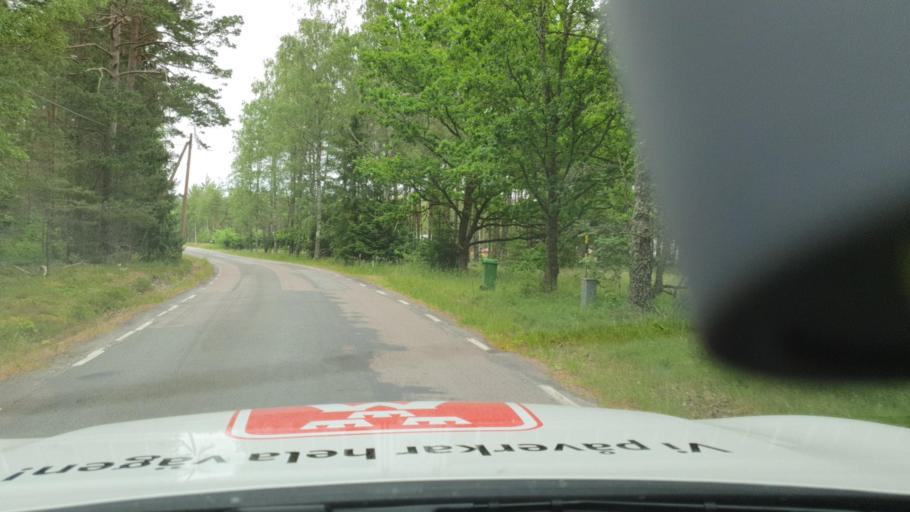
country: SE
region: Vaestra Goetaland
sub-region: Karlsborgs Kommun
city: Molltorp
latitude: 58.4231
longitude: 14.3708
